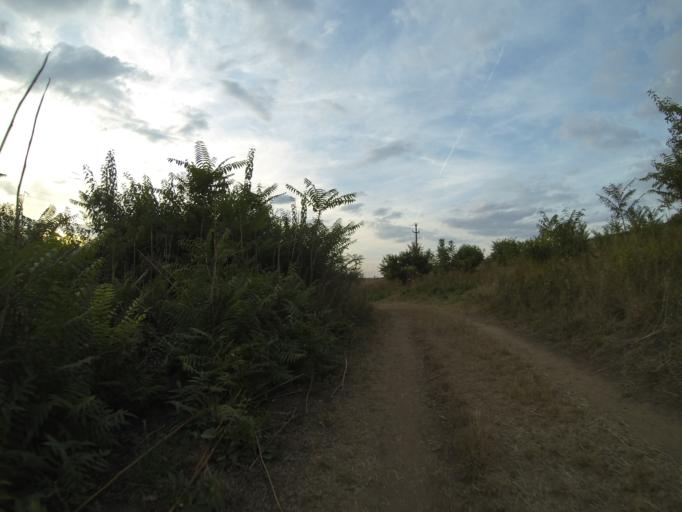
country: RO
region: Dolj
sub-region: Comuna Ceratu
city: Ceratu
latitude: 44.0919
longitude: 23.6692
